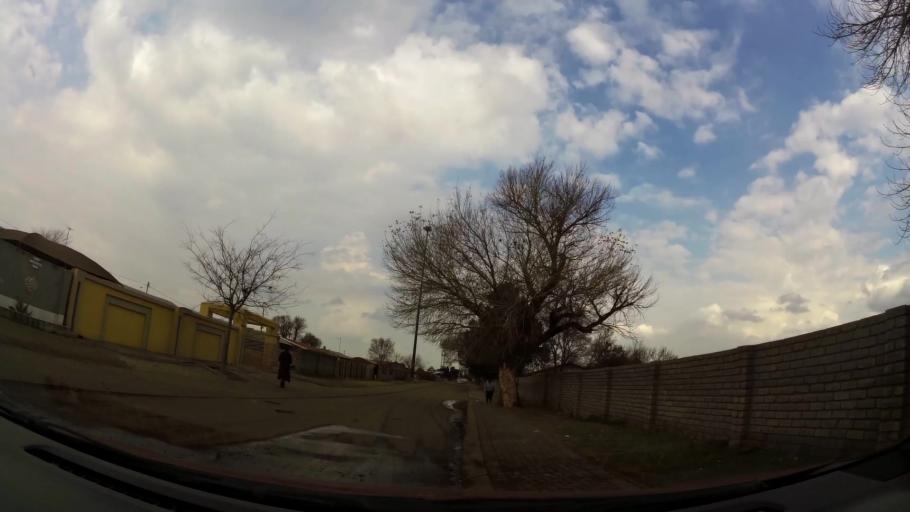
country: ZA
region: Gauteng
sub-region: Sedibeng District Municipality
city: Vanderbijlpark
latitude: -26.6661
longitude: 27.8464
